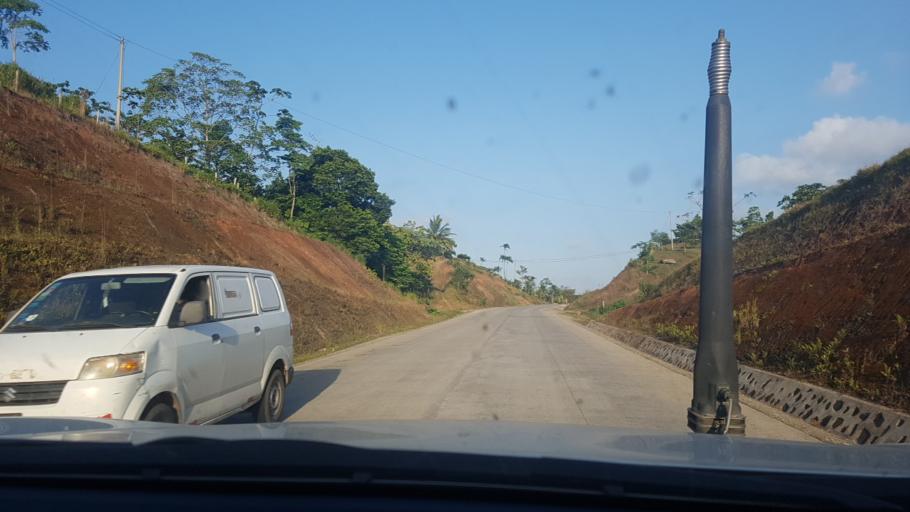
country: NI
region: Atlantico Sur
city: Nueva Guinea
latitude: 11.8068
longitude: -84.1147
